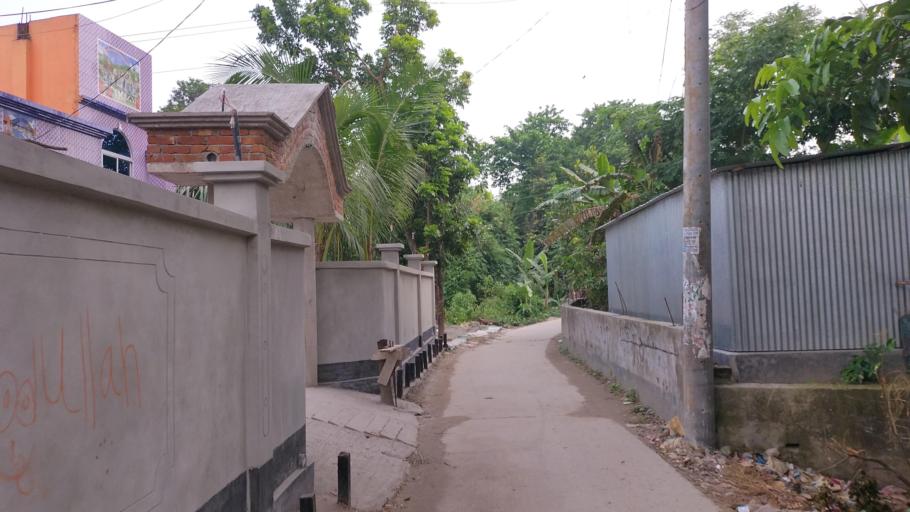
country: BD
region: Dhaka
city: Azimpur
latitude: 23.6796
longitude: 90.3149
